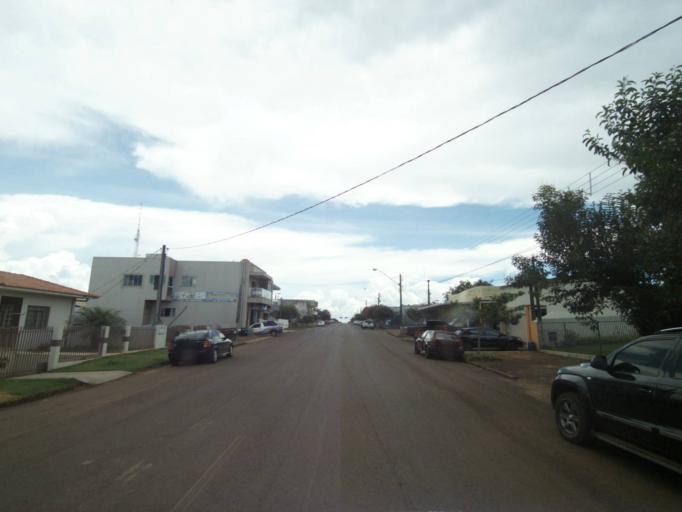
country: BR
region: Parana
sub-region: Guaraniacu
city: Guaraniacu
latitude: -25.1026
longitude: -52.8641
